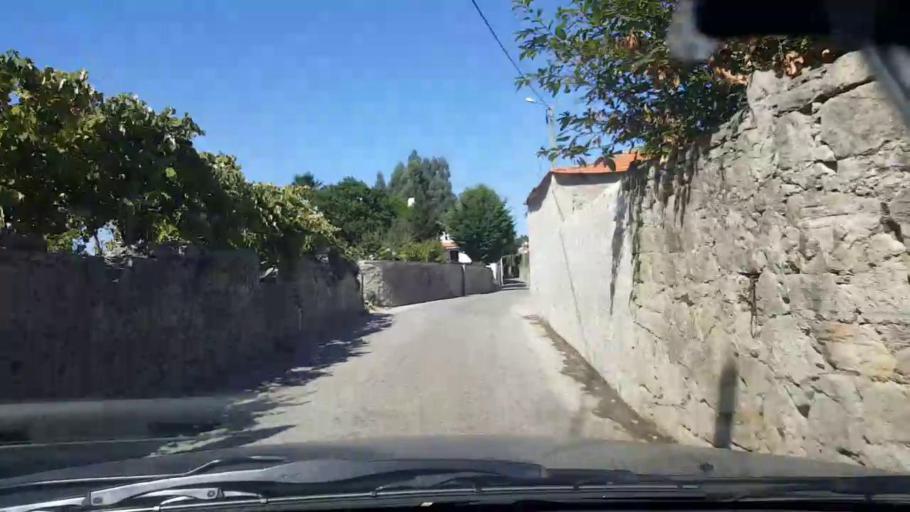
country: PT
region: Porto
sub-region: Vila do Conde
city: Arvore
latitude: 41.3143
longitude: -8.6730
